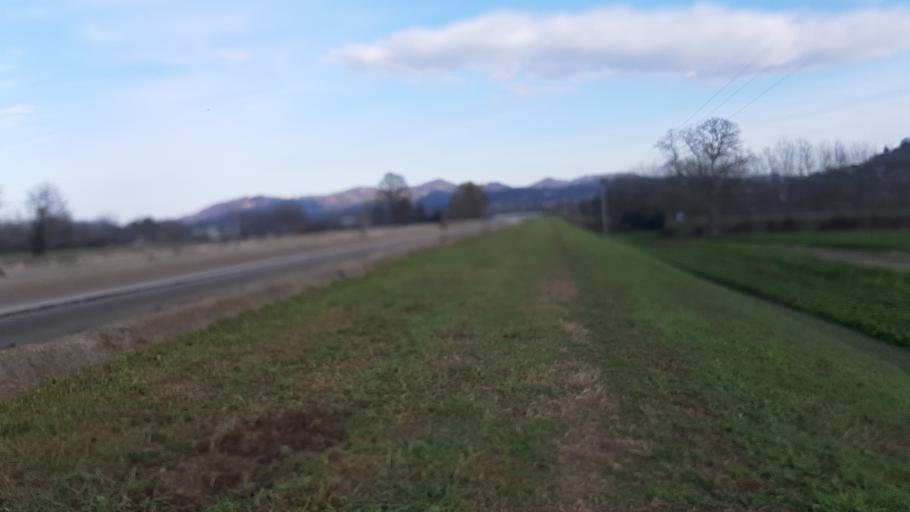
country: IT
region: Piedmont
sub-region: Provincia di Torino
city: Castiglione Torinese
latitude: 45.1247
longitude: 7.7998
